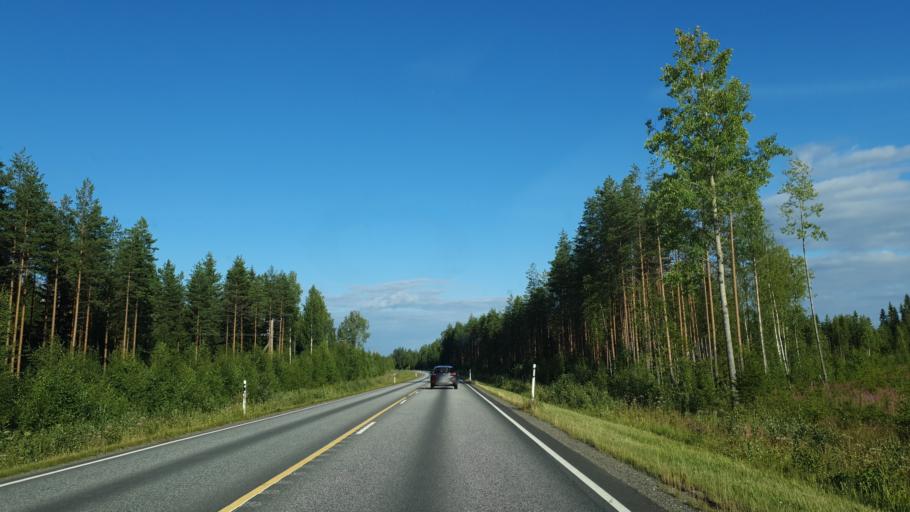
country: FI
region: North Karelia
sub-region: Joensuu
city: Outokumpu
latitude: 62.5343
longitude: 28.9522
